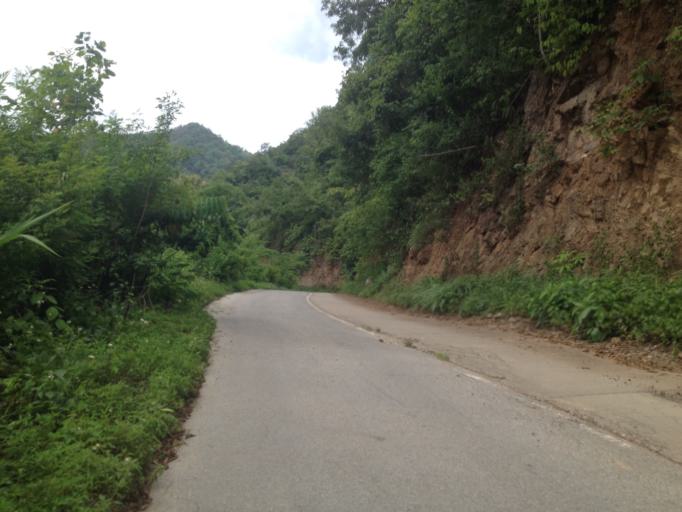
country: TH
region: Chiang Mai
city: Hang Dong
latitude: 18.7203
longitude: 98.8393
